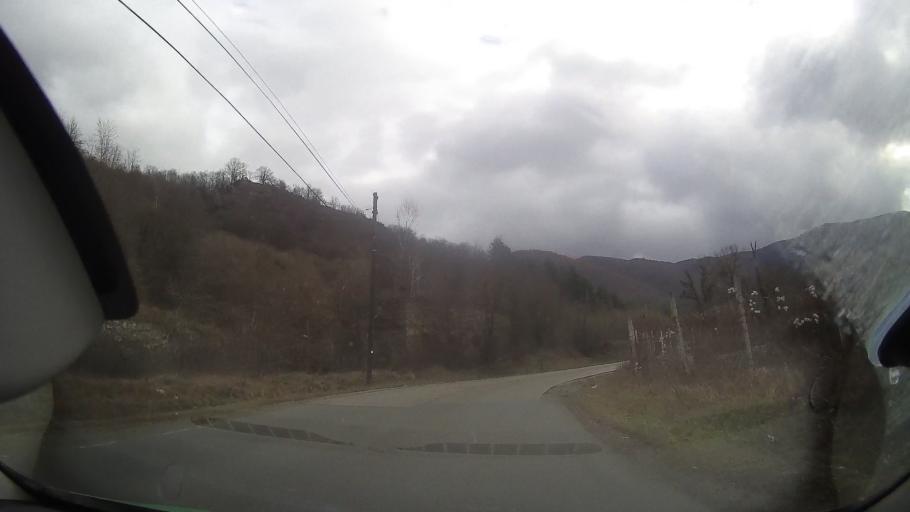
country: RO
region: Cluj
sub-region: Comuna Moldovenesti
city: Moldovenesti
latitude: 46.5087
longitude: 23.6050
